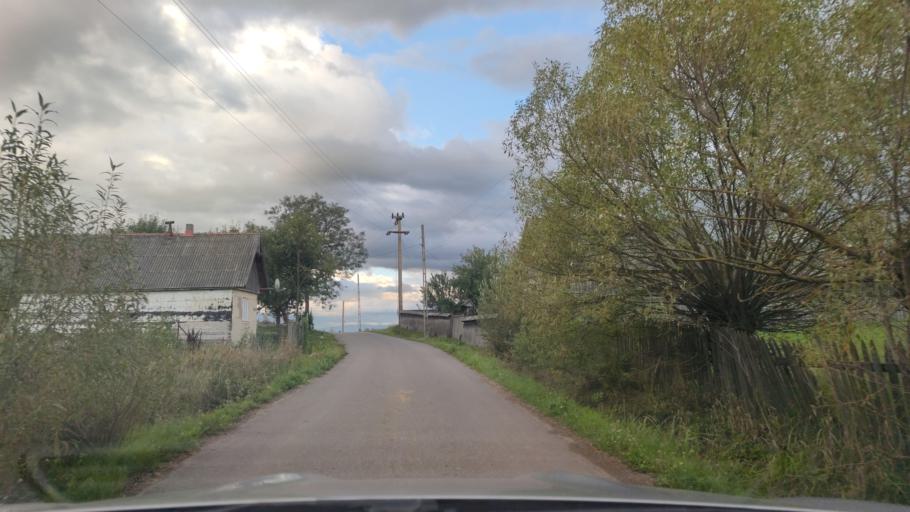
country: RO
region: Harghita
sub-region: Comuna Remetea
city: Remetea
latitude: 46.8097
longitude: 25.4367
